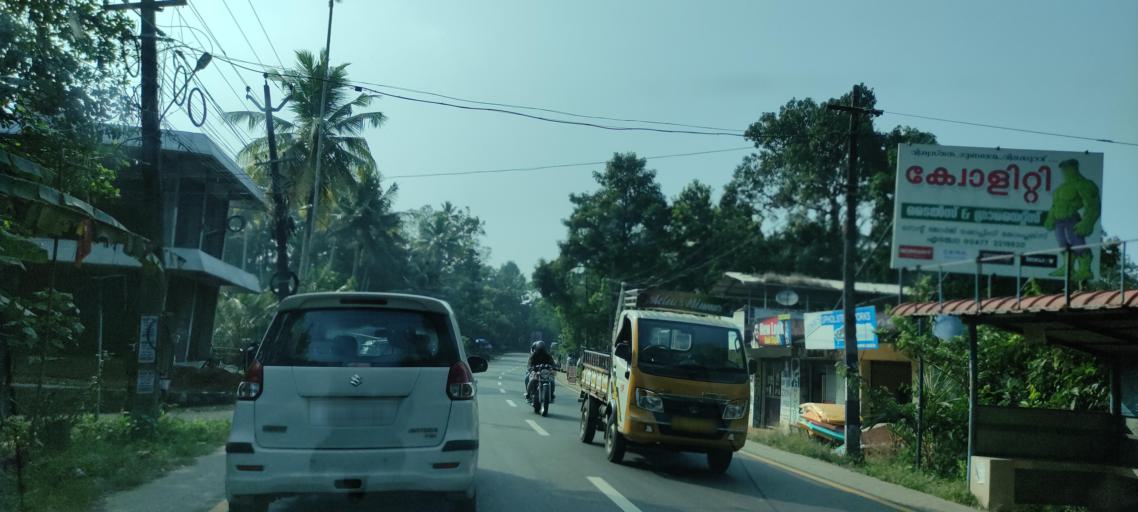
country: IN
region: Kerala
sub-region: Pattanamtitta
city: Tiruvalla
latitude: 9.3675
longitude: 76.5331
